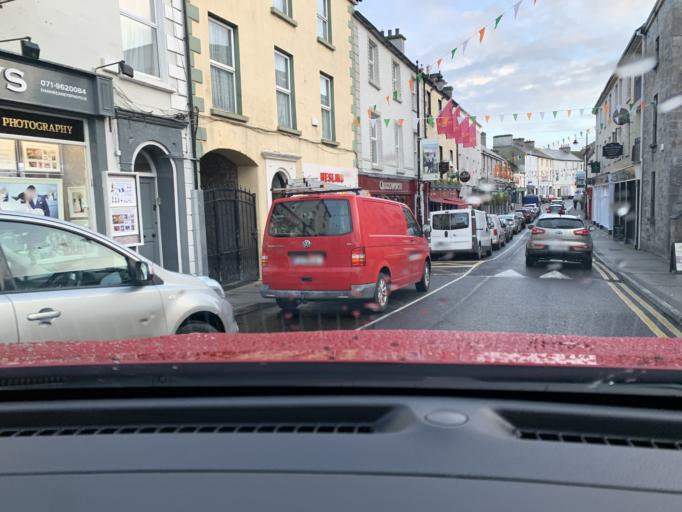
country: IE
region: Connaught
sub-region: County Leitrim
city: Carrick-on-Shannon
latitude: 53.9453
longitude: -8.0956
